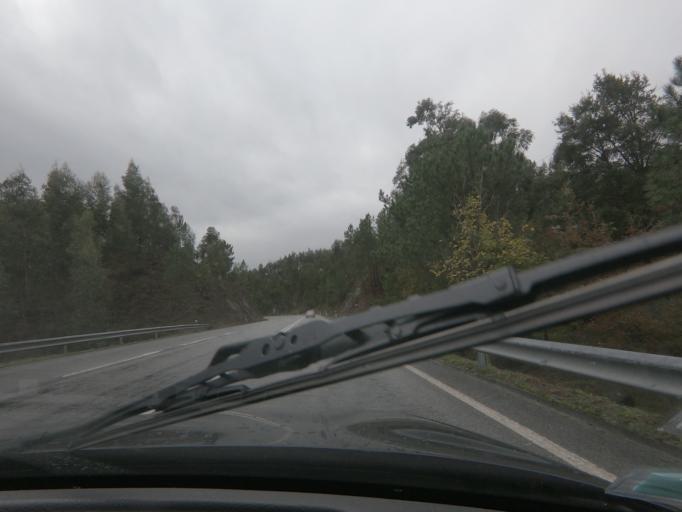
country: PT
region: Braga
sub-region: Celorico de Basto
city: Celorico de Basto
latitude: 41.3431
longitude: -8.0310
